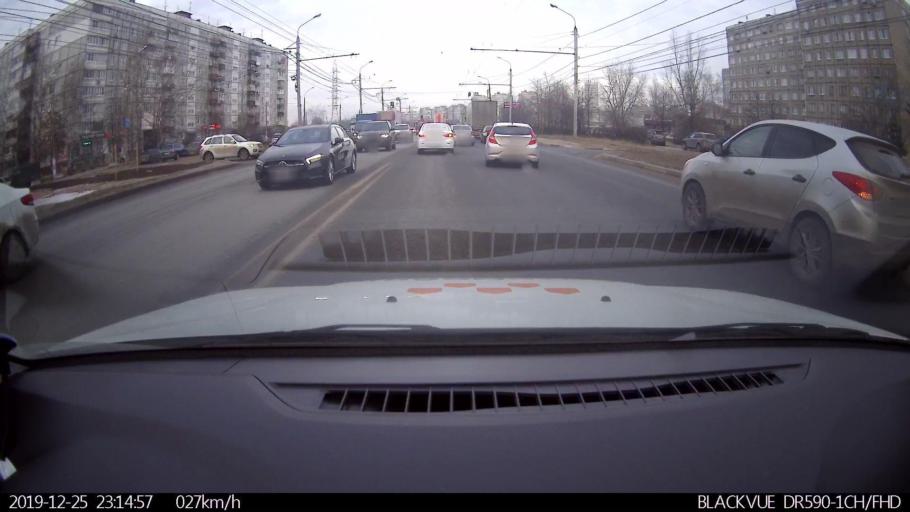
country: RU
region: Nizjnij Novgorod
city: Nizhniy Novgorod
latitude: 56.3366
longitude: 43.9209
